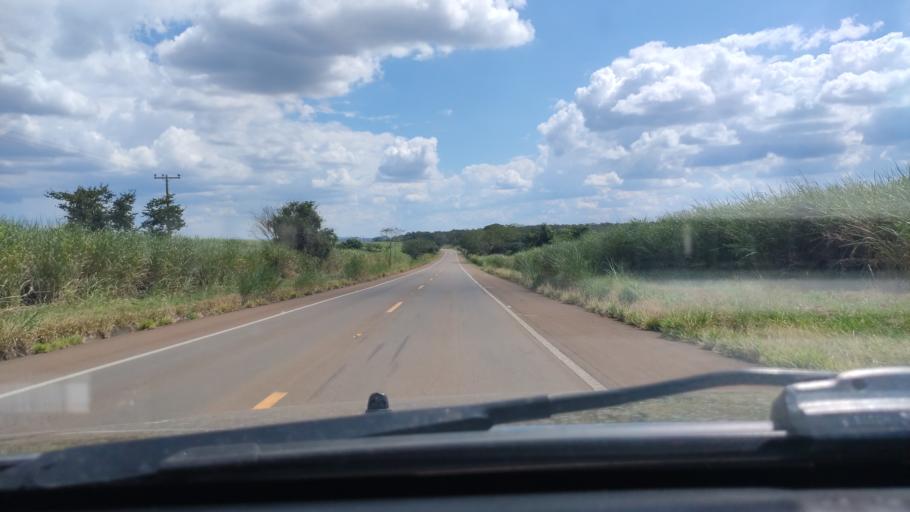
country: BR
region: Sao Paulo
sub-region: Ibate
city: Ibate
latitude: -22.0553
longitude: -48.0176
